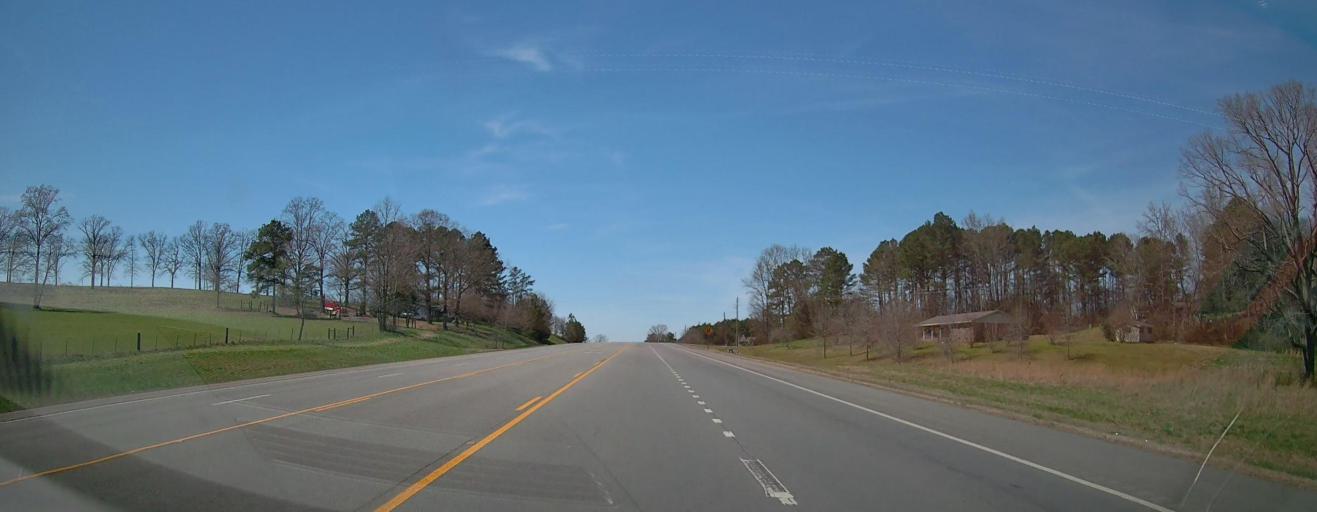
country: US
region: Alabama
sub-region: Blount County
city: Blountsville
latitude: 34.1682
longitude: -86.5196
